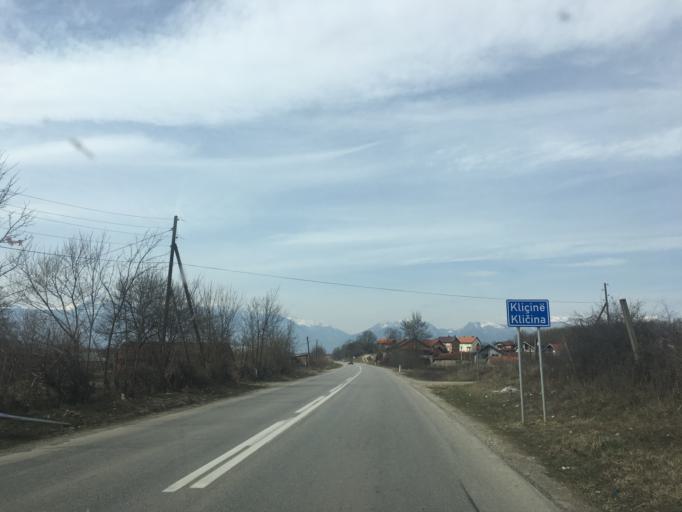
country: XK
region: Pec
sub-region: Komuna e Pejes
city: Kosuriq
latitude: 42.6227
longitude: 20.4724
